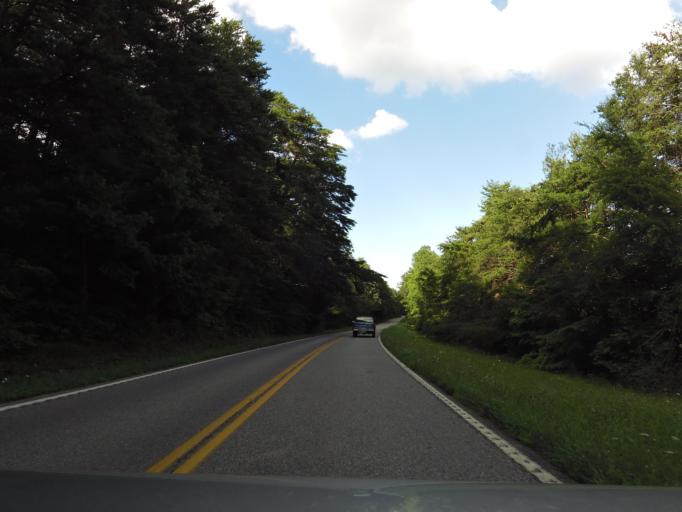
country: US
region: Tennessee
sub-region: Loudon County
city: Greenback
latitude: 35.6142
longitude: -84.0571
